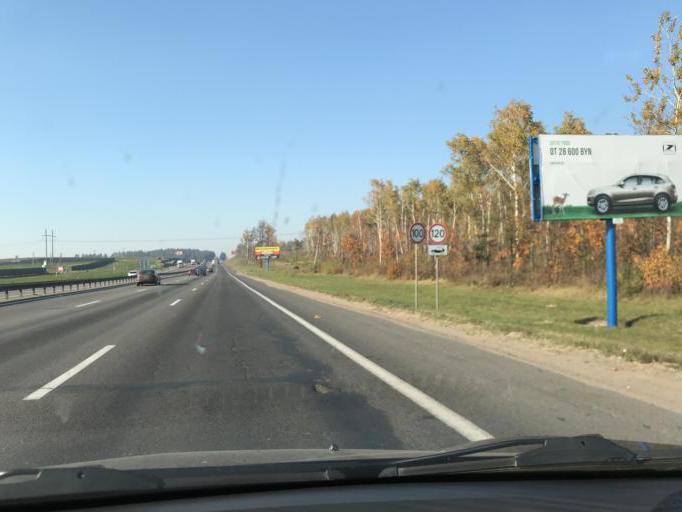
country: BY
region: Minsk
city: Pryvol'ny
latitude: 53.8101
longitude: 27.7829
